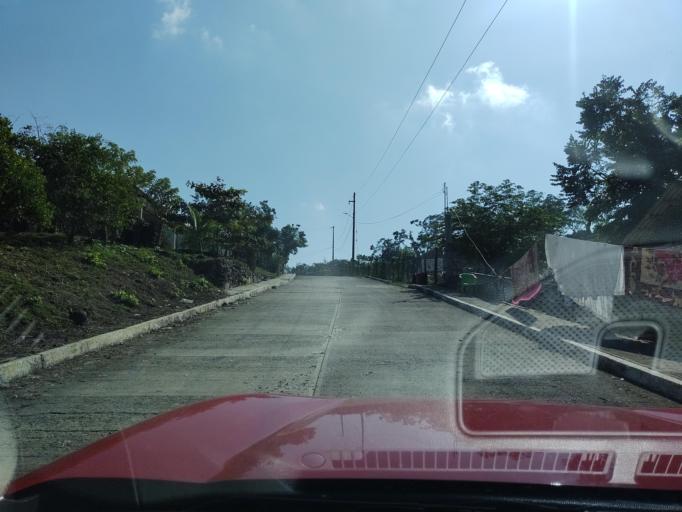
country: MX
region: Veracruz
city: Agua Dulce
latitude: 20.2878
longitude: -97.1850
